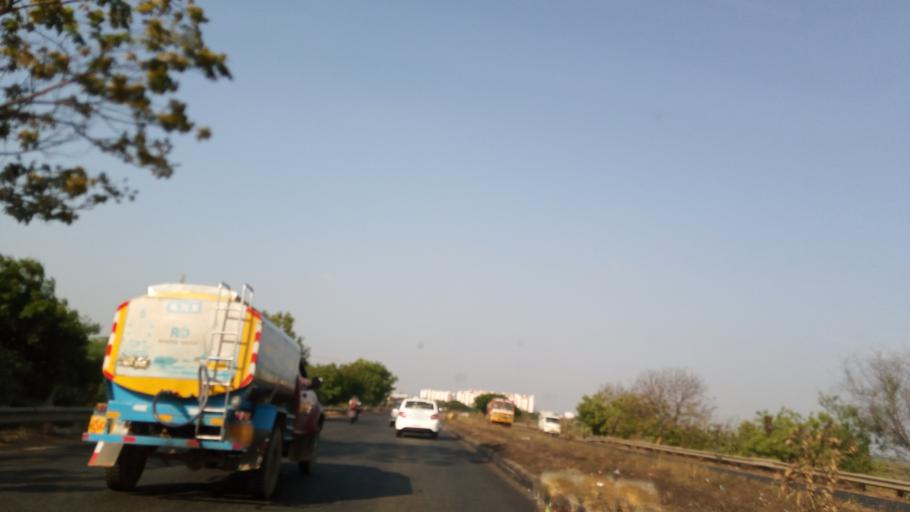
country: IN
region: Tamil Nadu
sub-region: Kancheepuram
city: Nandambakkam
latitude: 13.0196
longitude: 80.0127
